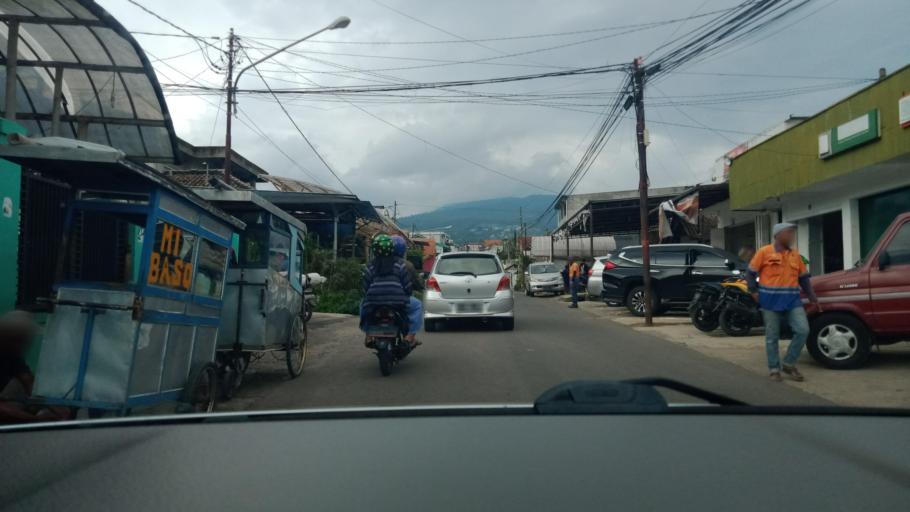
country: ID
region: West Java
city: Lembang
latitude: -6.8170
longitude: 107.5947
